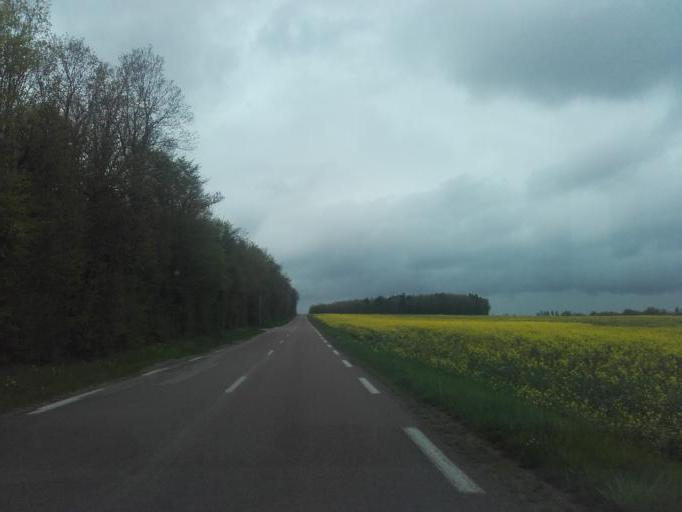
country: FR
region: Bourgogne
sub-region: Departement de l'Yonne
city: Joux-la-Ville
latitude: 47.6994
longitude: 3.8604
